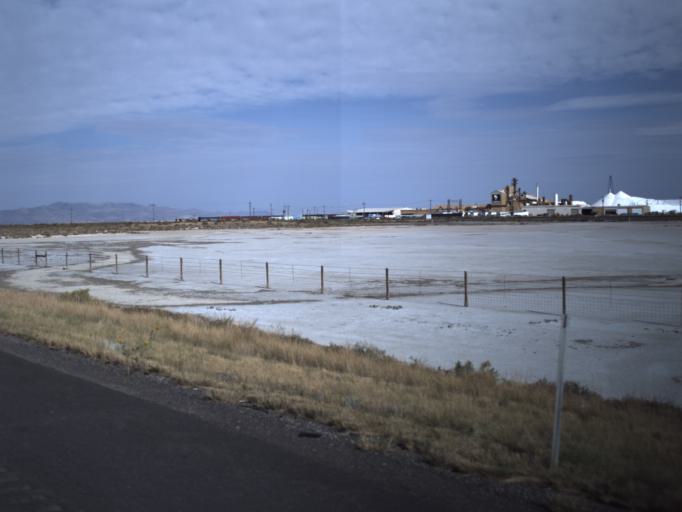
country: US
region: Utah
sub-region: Tooele County
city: Grantsville
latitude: 40.7041
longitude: -112.5054
